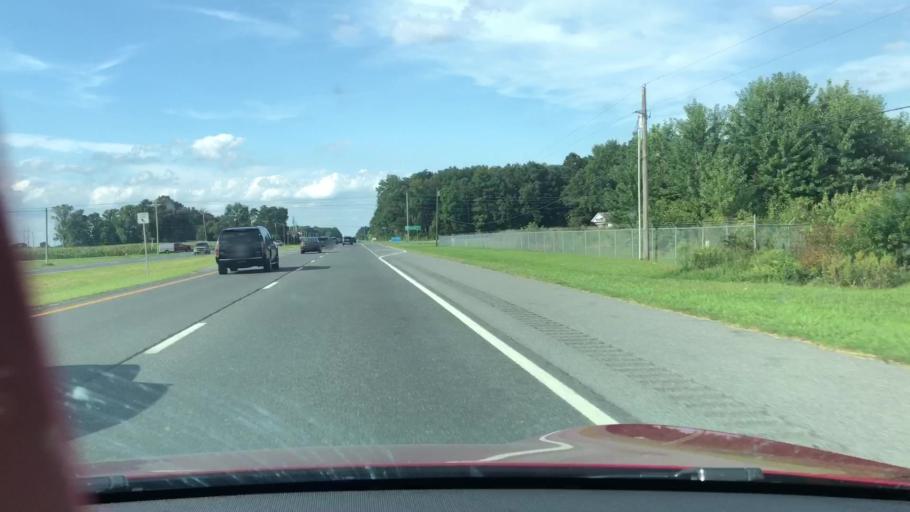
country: US
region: Delaware
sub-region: Kent County
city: Harrington
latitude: 38.8865
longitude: -75.5724
